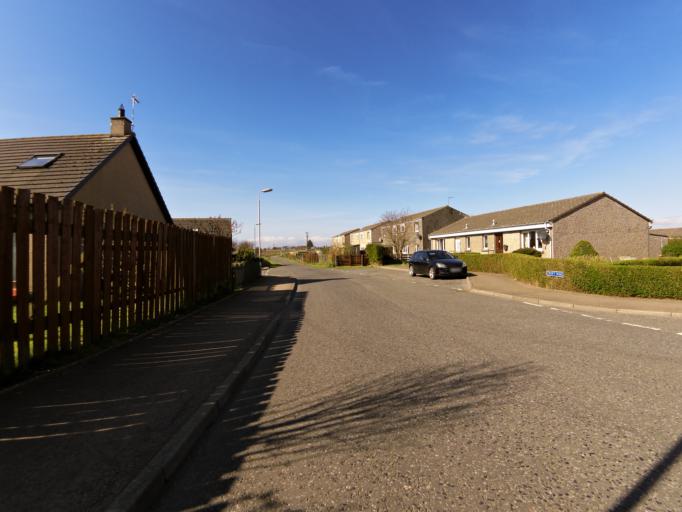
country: GB
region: Scotland
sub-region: Aberdeenshire
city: Laurencekirk
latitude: 56.7722
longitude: -2.4161
